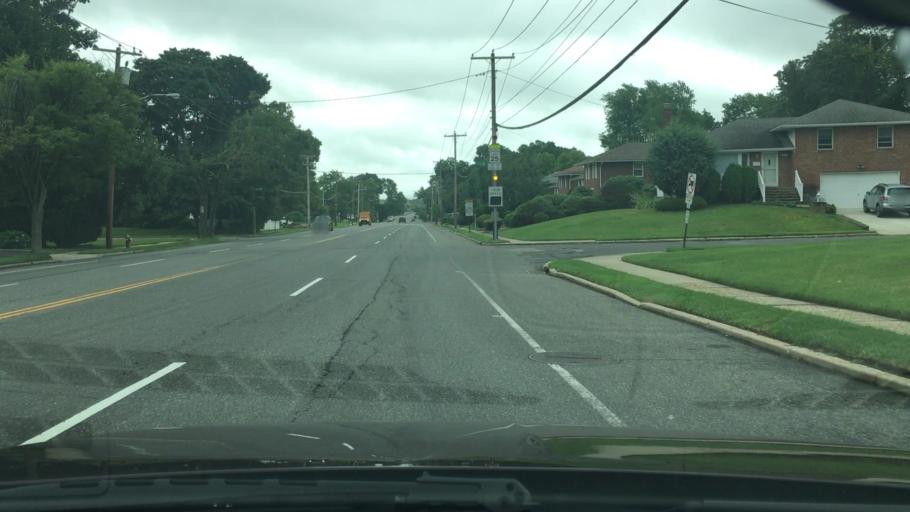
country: US
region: New York
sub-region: Nassau County
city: Jericho
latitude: 40.8020
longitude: -73.5272
